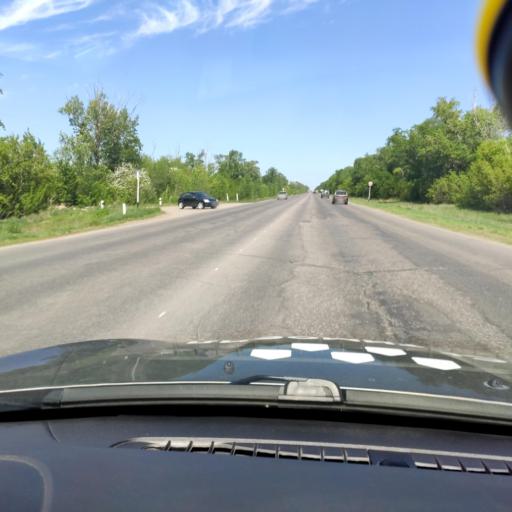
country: RU
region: Samara
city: Tol'yatti
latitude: 53.6051
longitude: 49.4103
